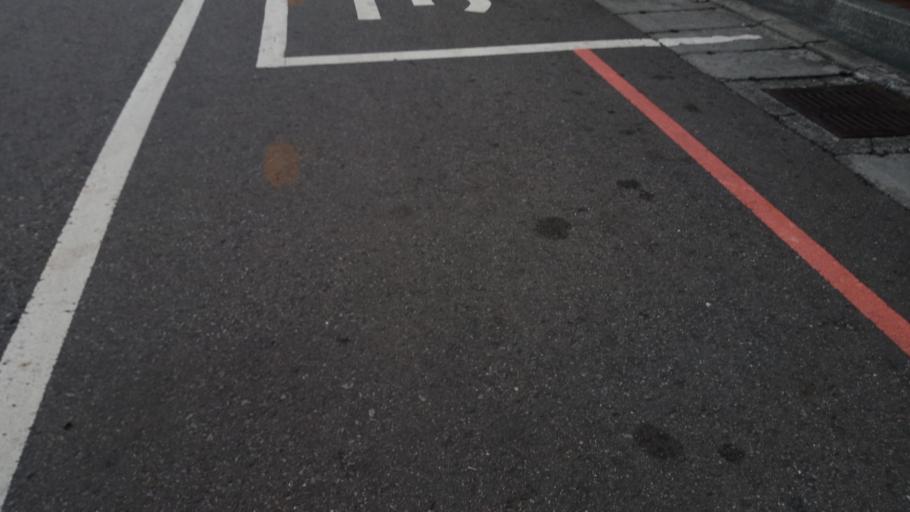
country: TW
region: Taiwan
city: Daxi
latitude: 24.9381
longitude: 121.2496
